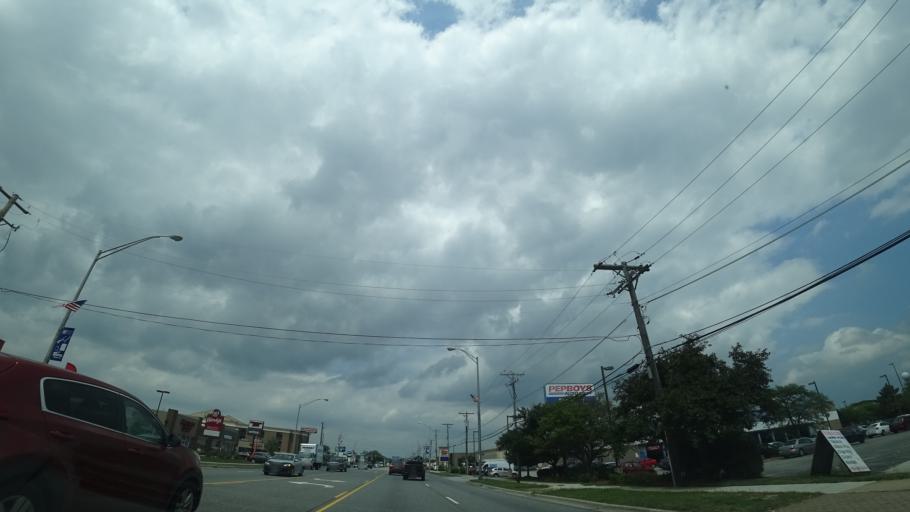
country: US
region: Illinois
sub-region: Cook County
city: Crestwood
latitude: 41.6484
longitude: -87.7381
